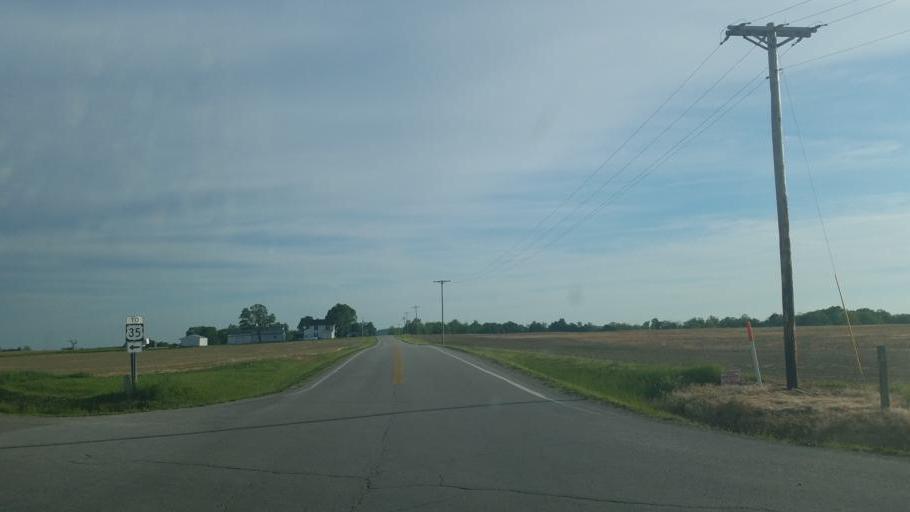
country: US
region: Ohio
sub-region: Ross County
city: Frankfort
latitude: 39.4442
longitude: -83.2189
